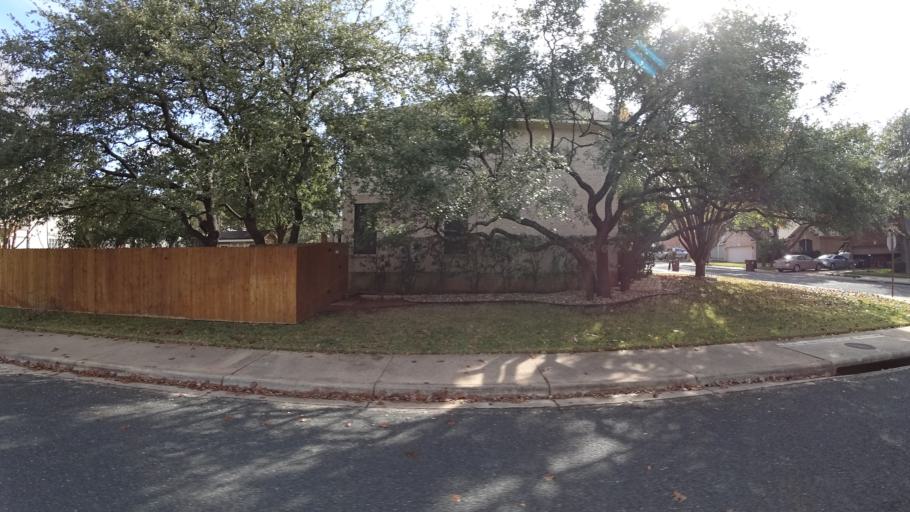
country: US
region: Texas
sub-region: Williamson County
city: Brushy Creek
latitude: 30.5172
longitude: -97.7392
